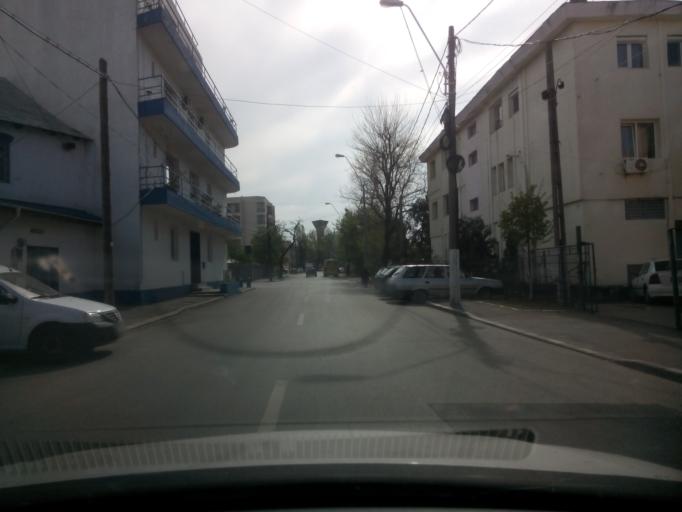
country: RO
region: Bucuresti
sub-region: Municipiul Bucuresti
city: Bucharest
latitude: 44.4534
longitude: 26.1309
